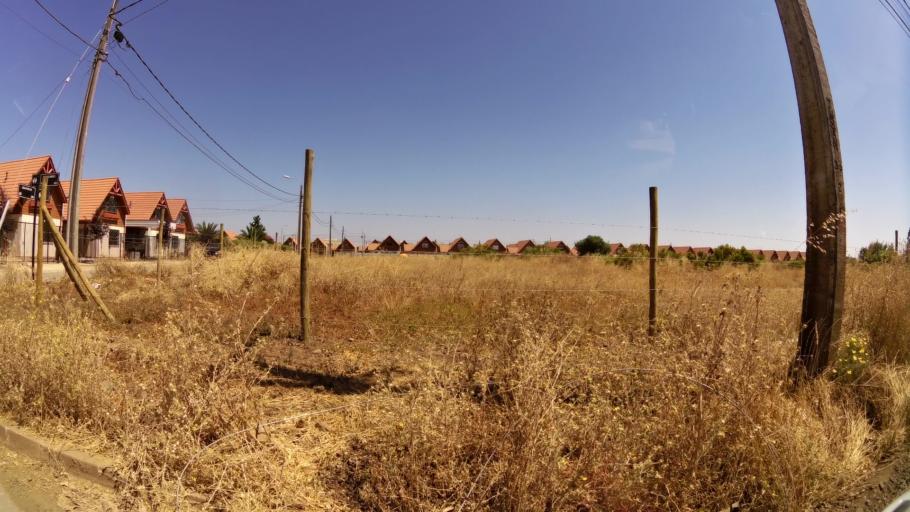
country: CL
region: Maule
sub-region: Provincia de Talca
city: Talca
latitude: -35.4287
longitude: -71.6086
